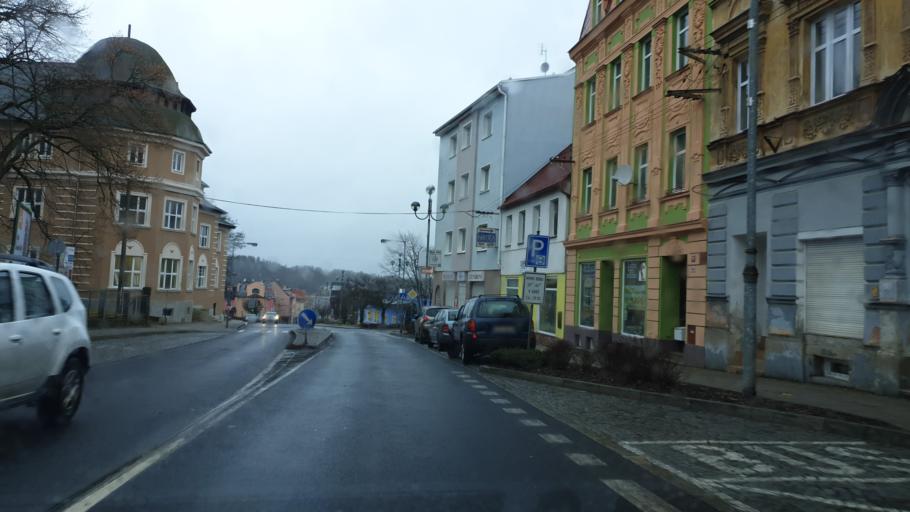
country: CZ
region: Karlovarsky
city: As
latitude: 50.2184
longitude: 12.1942
